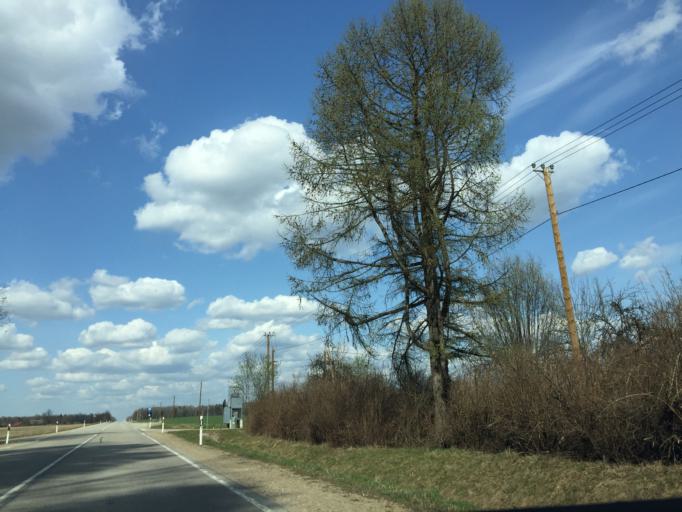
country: LV
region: Skriveri
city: Skriveri
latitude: 56.7656
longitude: 25.1689
